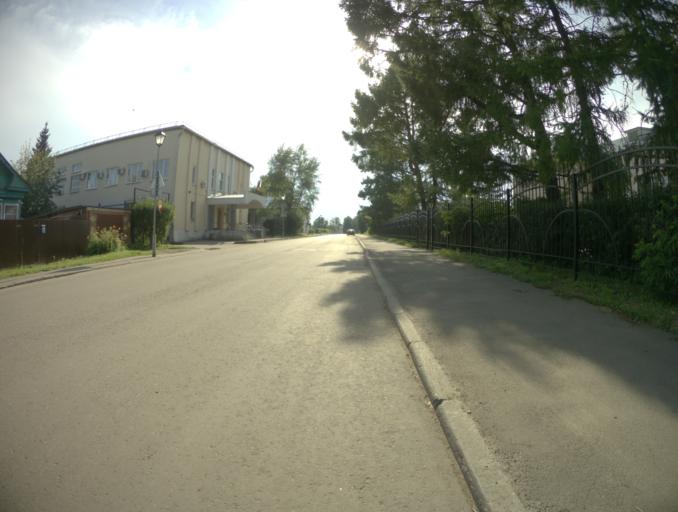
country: RU
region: Vladimir
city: Suzdal'
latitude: 56.4264
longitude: 40.4510
